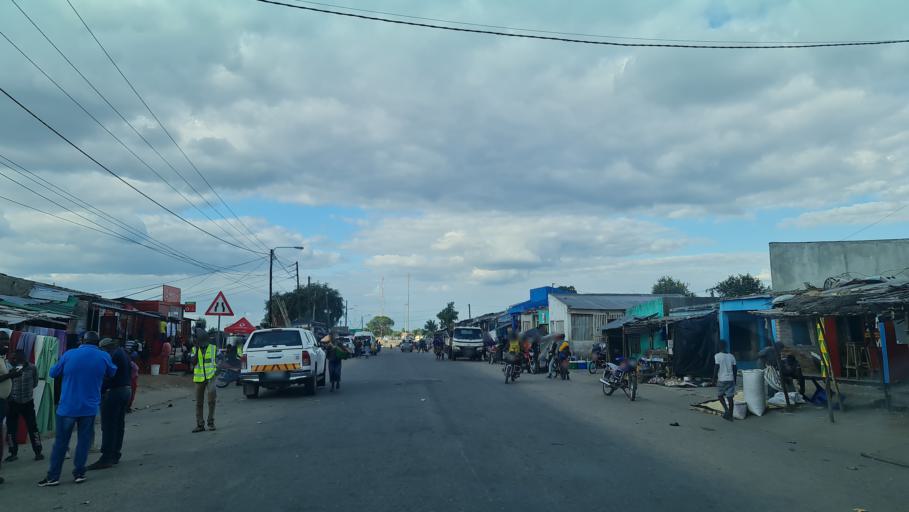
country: MZ
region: Manica
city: Chimoio
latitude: -19.2094
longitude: 33.9289
